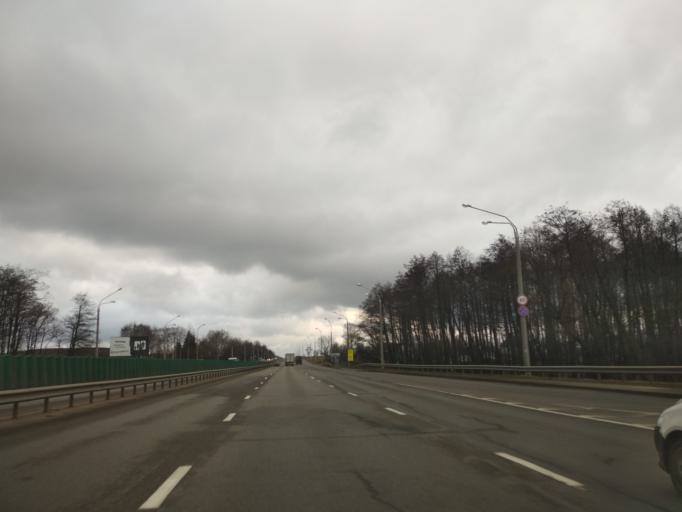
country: BY
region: Minsk
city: Vyaliki Trastsyanets
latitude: 53.8449
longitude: 27.7117
